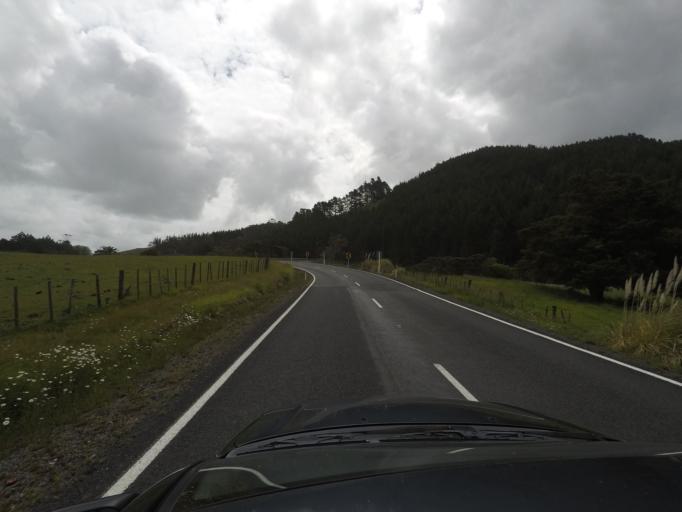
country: NZ
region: Auckland
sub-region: Auckland
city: Parakai
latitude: -36.5018
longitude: 174.4766
